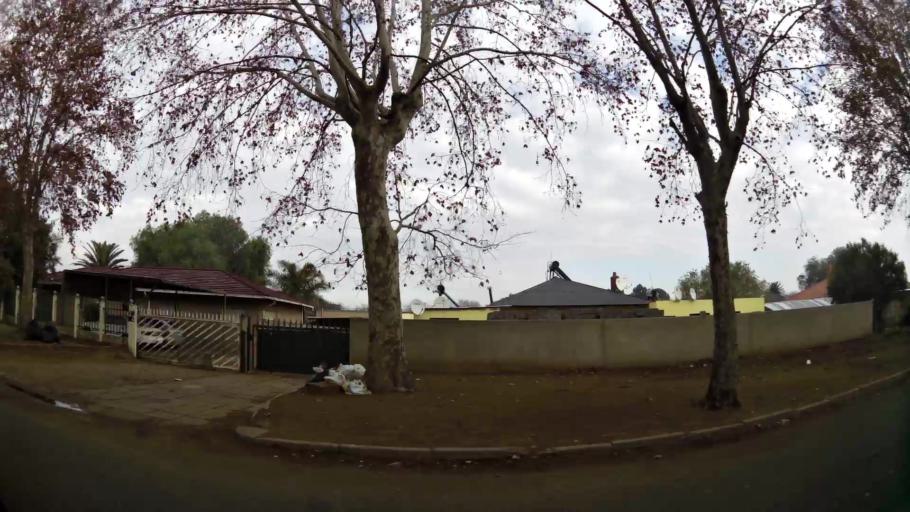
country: ZA
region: Gauteng
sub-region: Sedibeng District Municipality
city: Vanderbijlpark
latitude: -26.6876
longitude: 27.8152
